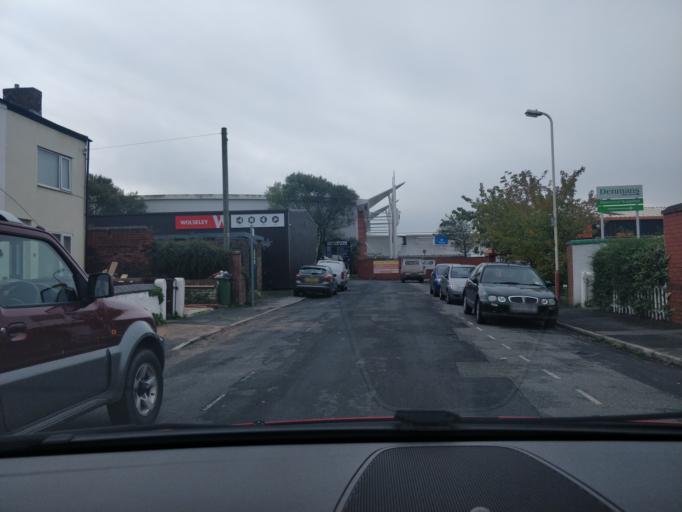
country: GB
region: England
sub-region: Sefton
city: Southport
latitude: 53.6454
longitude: -2.9941
